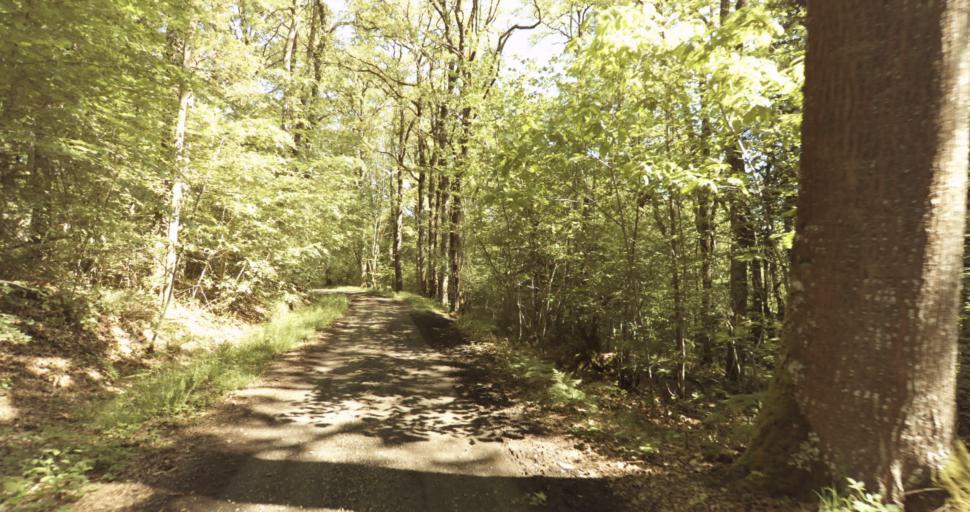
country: FR
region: Limousin
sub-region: Departement de la Haute-Vienne
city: Le Vigen
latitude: 45.7266
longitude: 1.3030
